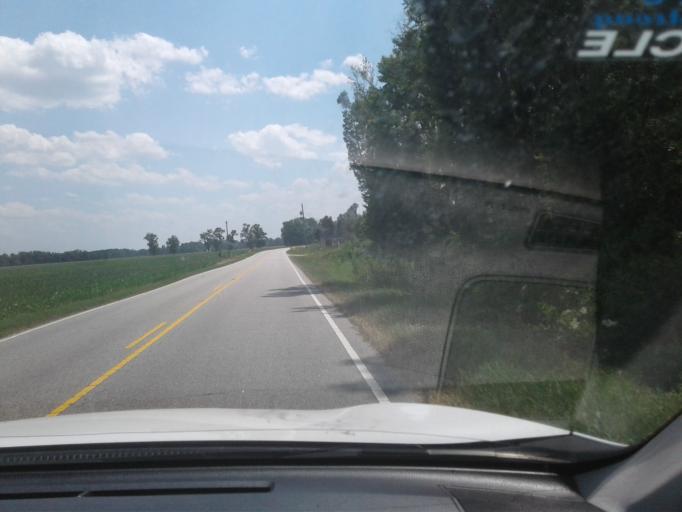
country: US
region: North Carolina
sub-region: Harnett County
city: Erwin
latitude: 35.2597
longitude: -78.6756
